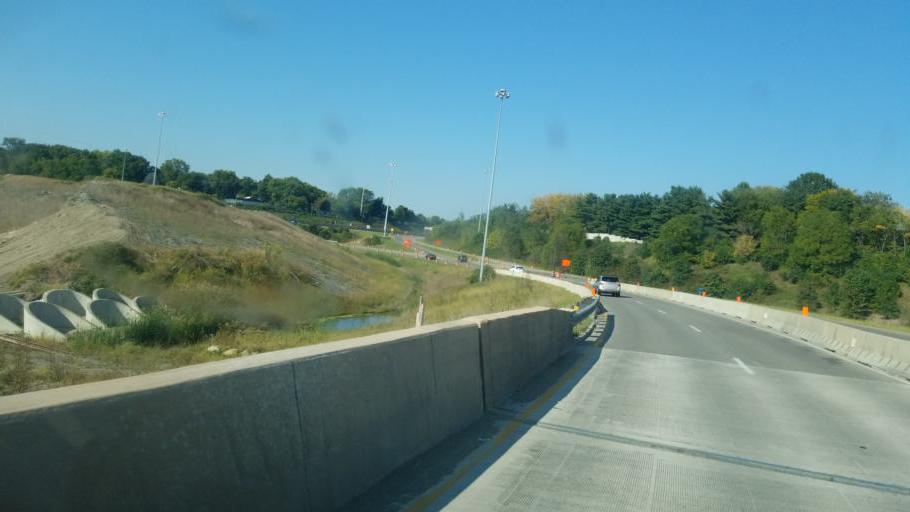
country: US
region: Ohio
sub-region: Franklin County
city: Worthington
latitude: 40.1140
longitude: -83.0350
